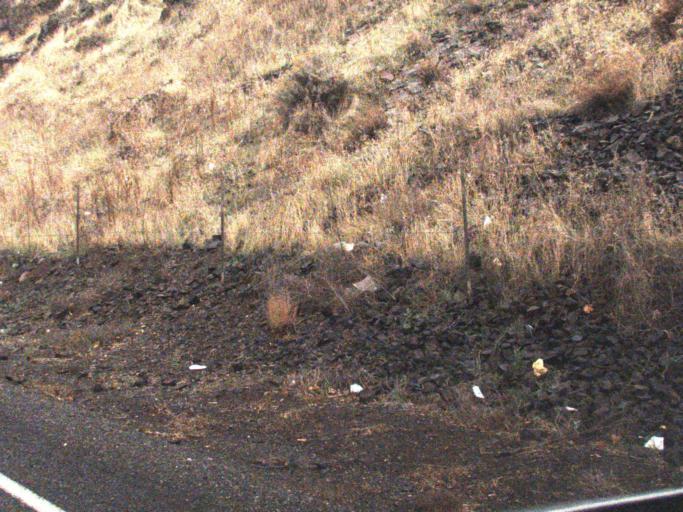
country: US
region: Washington
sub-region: Asotin County
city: Clarkston
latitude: 46.4316
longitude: -117.0411
